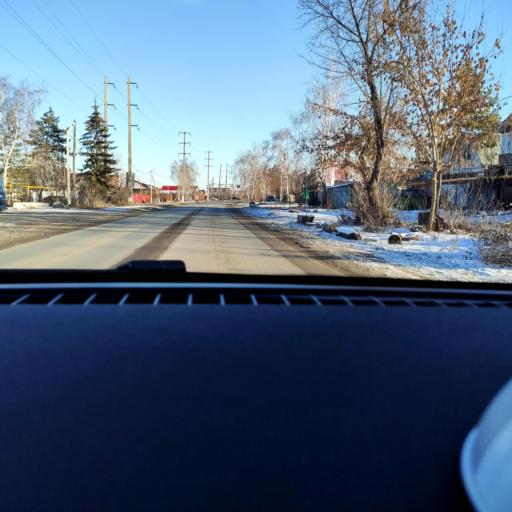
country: RU
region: Samara
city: Novokuybyshevsk
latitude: 53.1256
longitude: 49.9169
